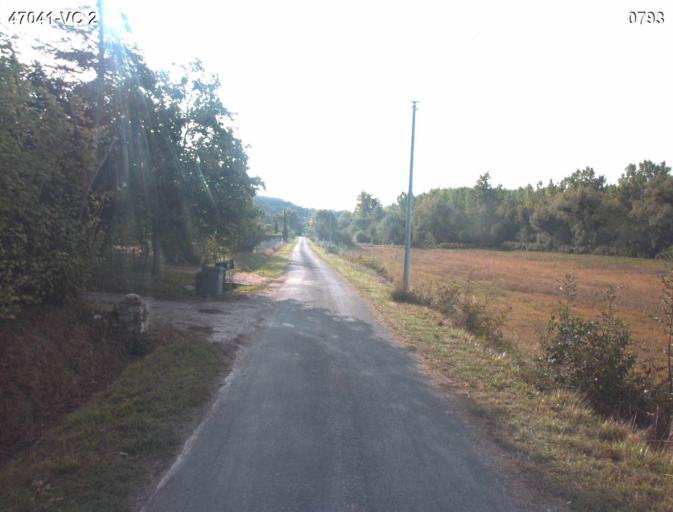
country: FR
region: Aquitaine
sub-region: Departement du Lot-et-Garonne
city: Port-Sainte-Marie
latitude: 44.1953
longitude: 0.4118
